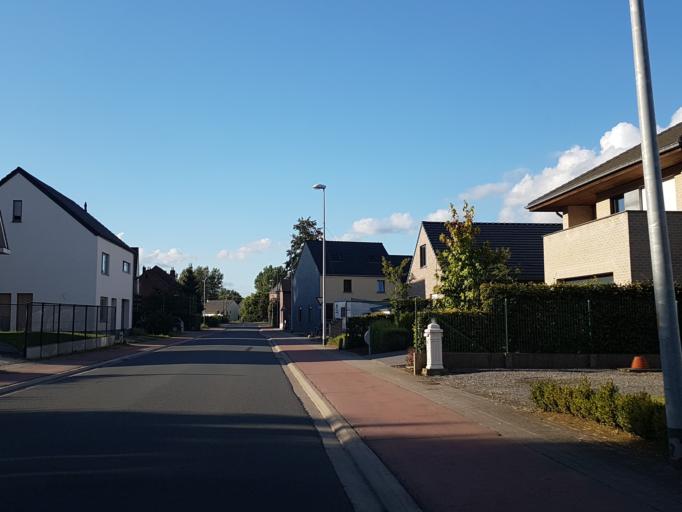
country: BE
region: Flanders
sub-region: Provincie Vlaams-Brabant
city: Herent
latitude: 50.9300
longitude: 4.6307
